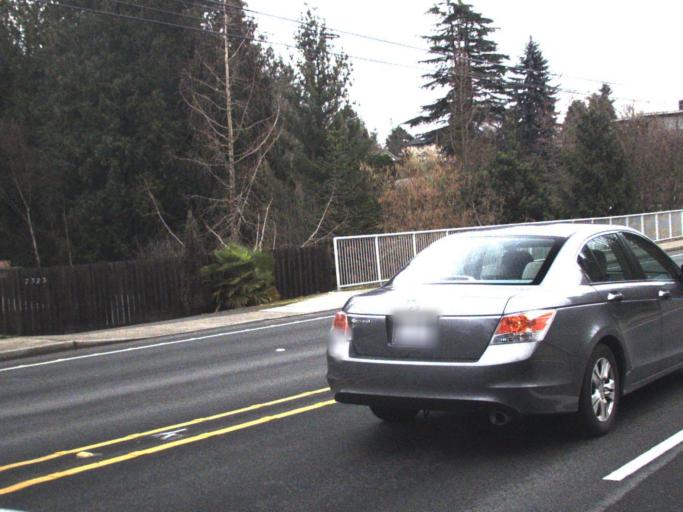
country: US
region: Washington
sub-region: Snohomish County
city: Marysville
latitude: 48.0537
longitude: -122.1318
